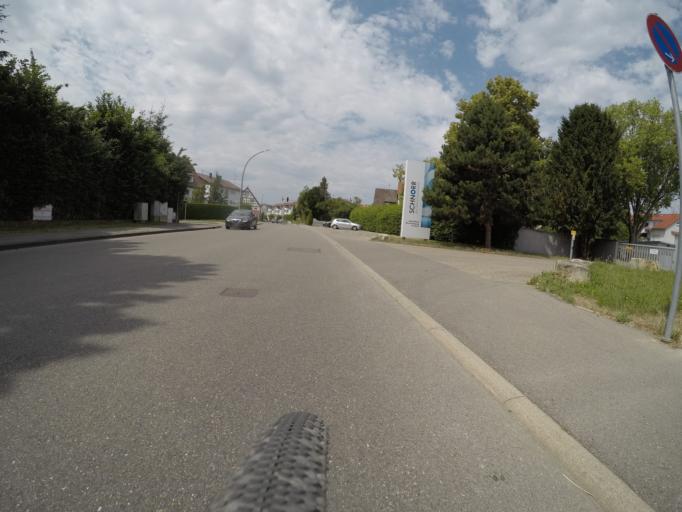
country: DE
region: Baden-Wuerttemberg
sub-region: Regierungsbezirk Stuttgart
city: Magstadt
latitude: 48.7264
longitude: 8.9696
